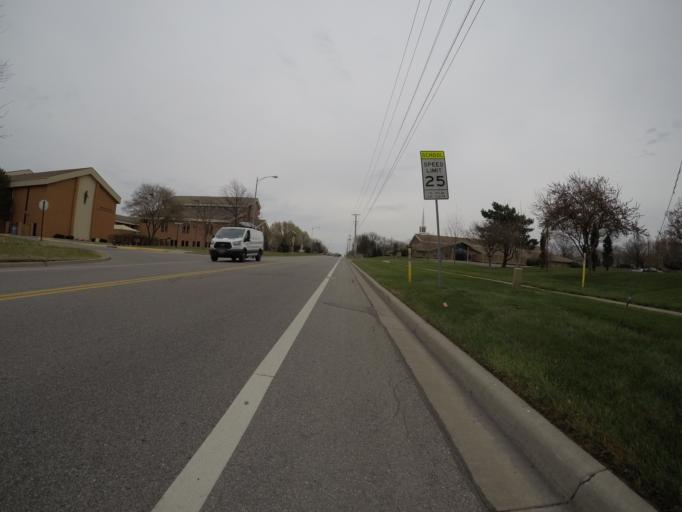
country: US
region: Kansas
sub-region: Johnson County
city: Olathe
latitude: 38.8691
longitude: -94.7723
